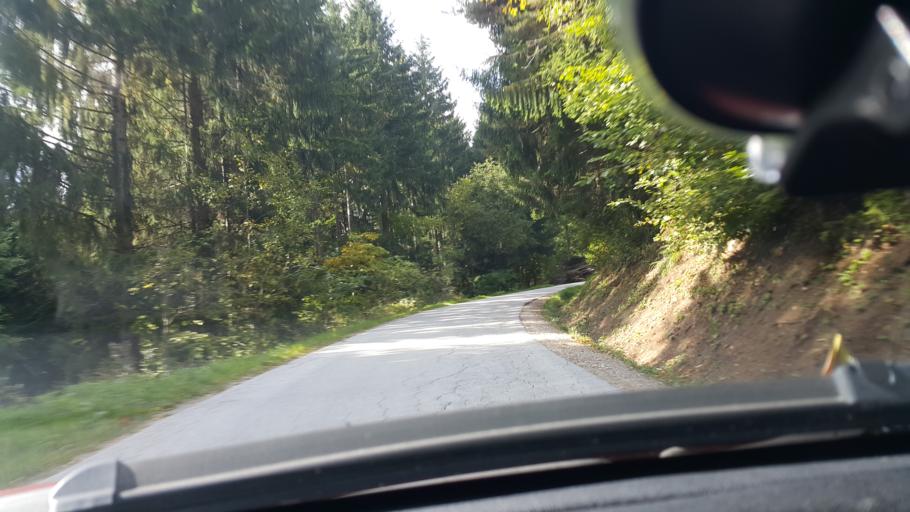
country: SI
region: Vitanje
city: Vitanje
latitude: 46.4056
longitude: 15.2907
